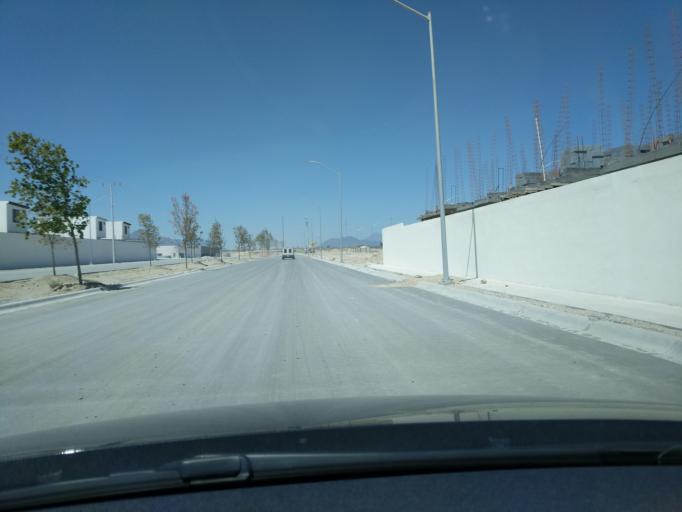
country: MX
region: Nuevo Leon
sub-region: Apodaca
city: Artemio Trevino
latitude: 25.8438
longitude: -100.1423
